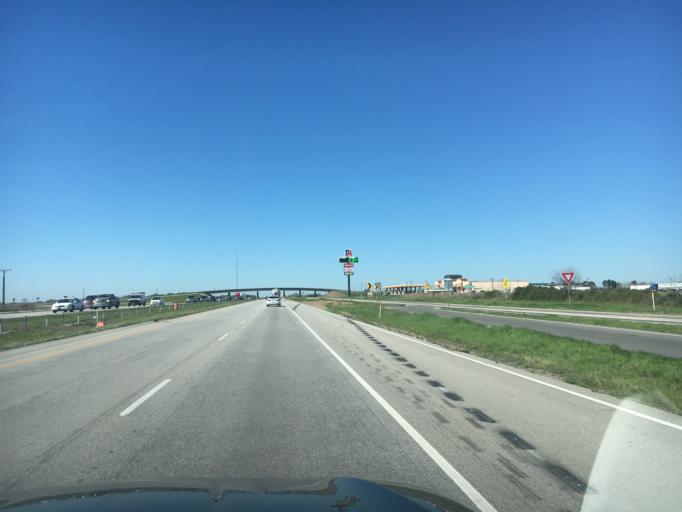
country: US
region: Texas
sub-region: Colorado County
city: Eagle Lake
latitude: 29.7425
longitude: -96.3263
